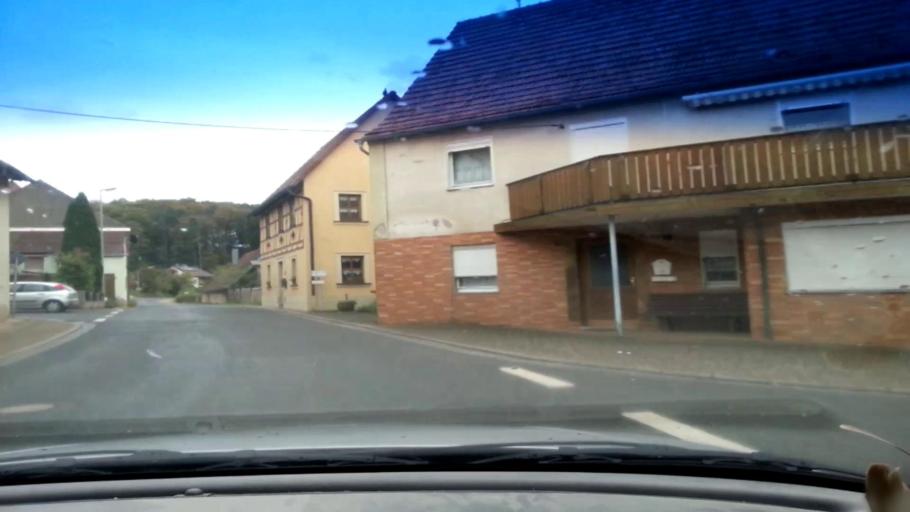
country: DE
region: Bavaria
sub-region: Regierungsbezirk Unterfranken
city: Stettfeld
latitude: 49.9995
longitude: 10.7459
